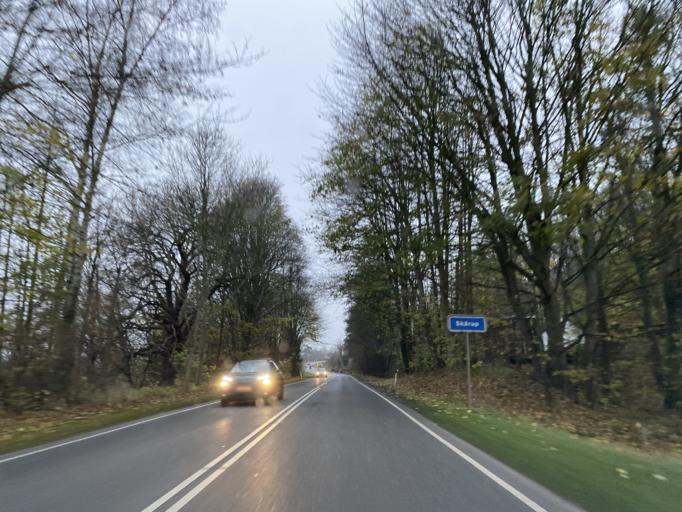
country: DK
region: Central Jutland
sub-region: Skanderborg Kommune
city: Stilling
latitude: 56.0150
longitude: 9.9855
